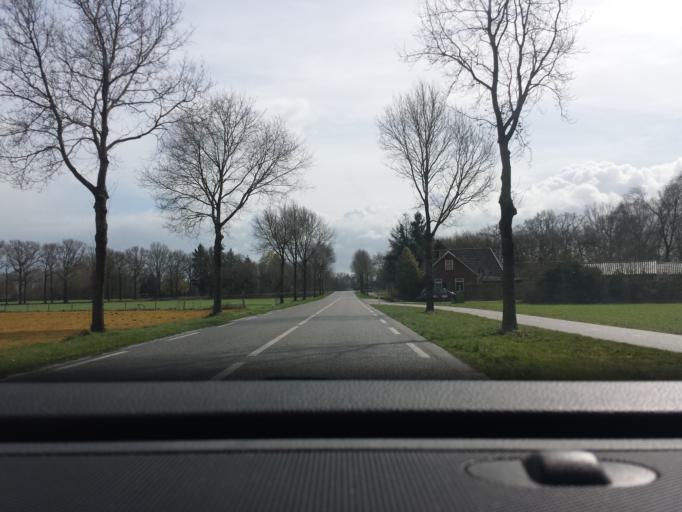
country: NL
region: Gelderland
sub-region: Oude IJsselstreek
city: Varsseveld
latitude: 51.9587
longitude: 6.4555
